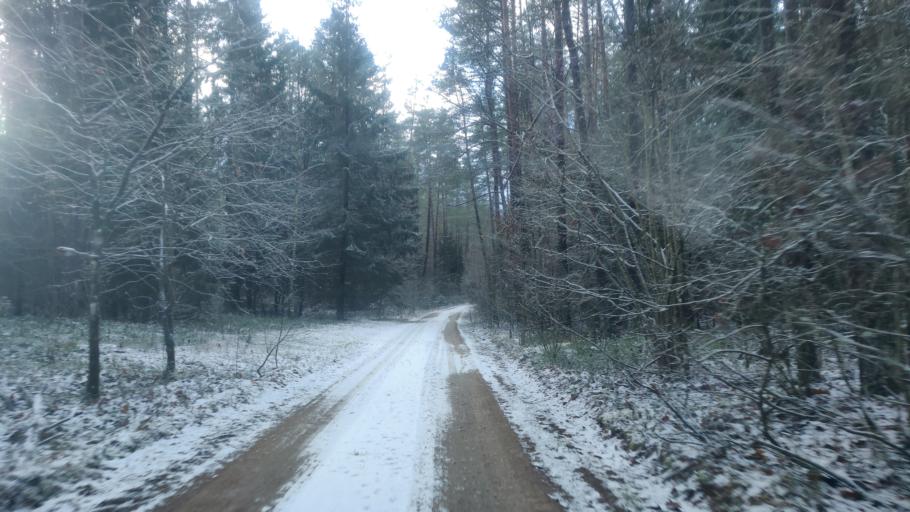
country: LT
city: Trakai
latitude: 54.5655
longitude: 24.9188
